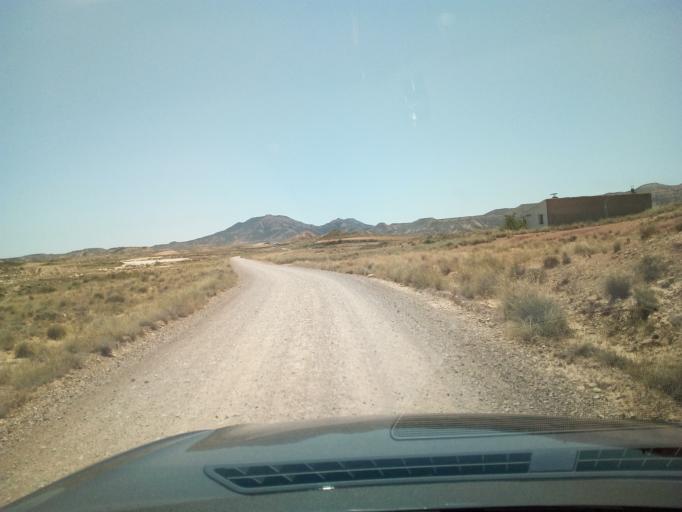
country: ES
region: Navarre
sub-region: Provincia de Navarra
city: Arguedas
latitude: 42.1709
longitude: -1.4457
